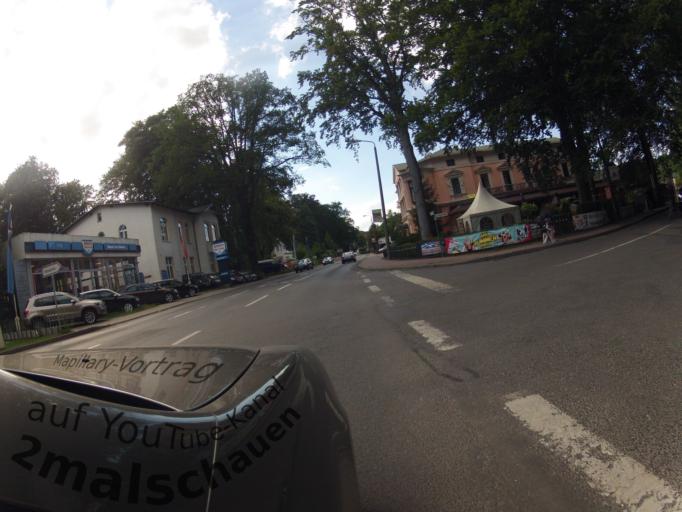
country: DE
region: Mecklenburg-Vorpommern
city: Seebad Heringsdorf
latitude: 53.9509
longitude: 14.1679
